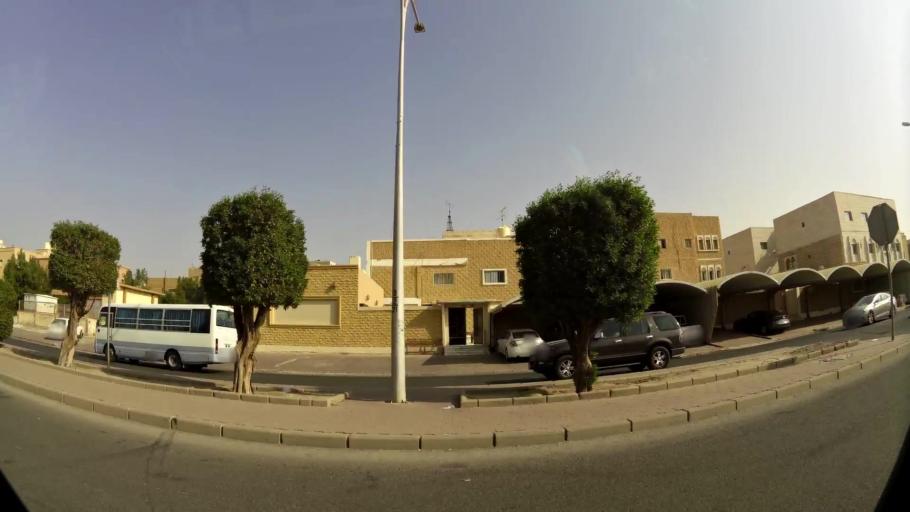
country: KW
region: Muhafazat al Jahra'
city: Al Jahra'
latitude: 29.3365
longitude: 47.7000
